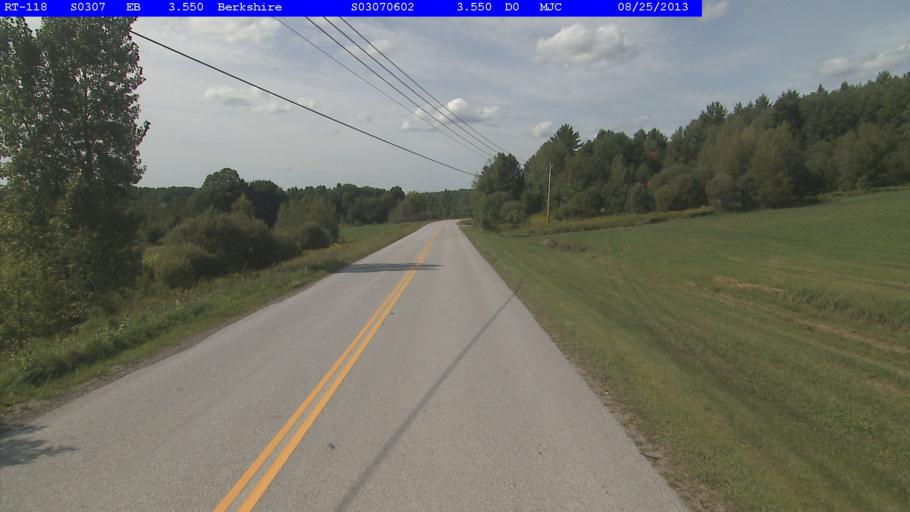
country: US
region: Vermont
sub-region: Franklin County
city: Enosburg Falls
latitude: 44.9664
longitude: -72.7605
